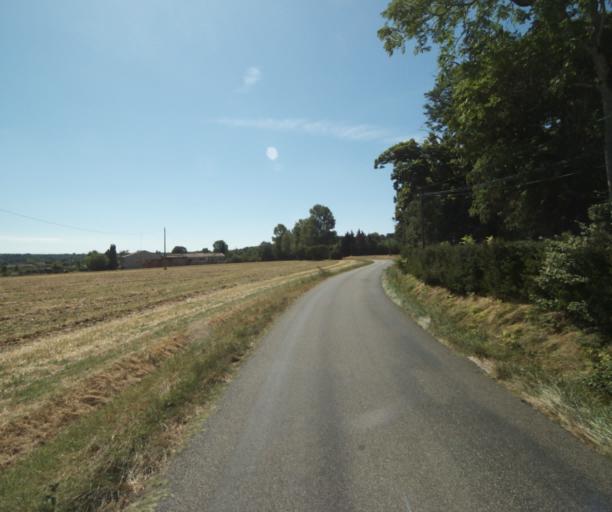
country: FR
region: Midi-Pyrenees
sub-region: Departement de la Haute-Garonne
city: Saint-Felix-Lauragais
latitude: 43.4940
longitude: 1.9398
